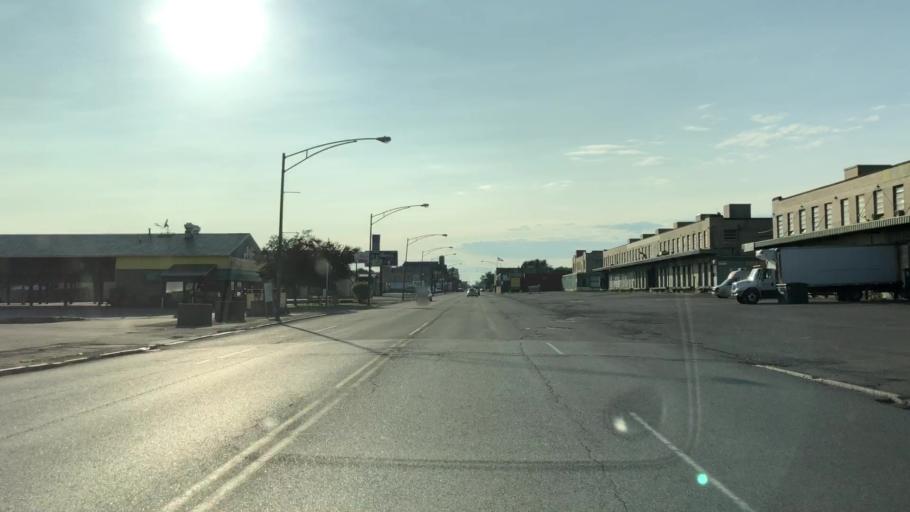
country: US
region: New York
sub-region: Erie County
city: West Seneca
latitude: 42.8724
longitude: -78.8209
